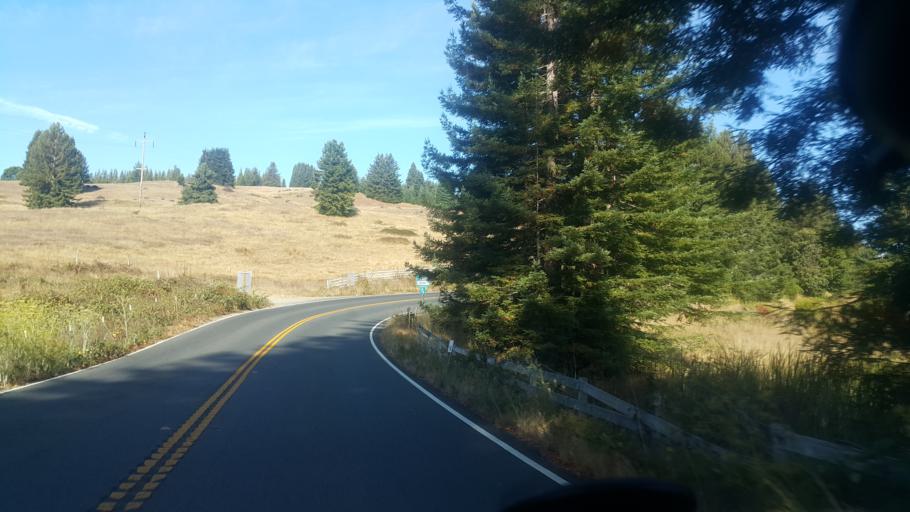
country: US
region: California
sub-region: Mendocino County
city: Fort Bragg
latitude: 39.3540
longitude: -123.6137
